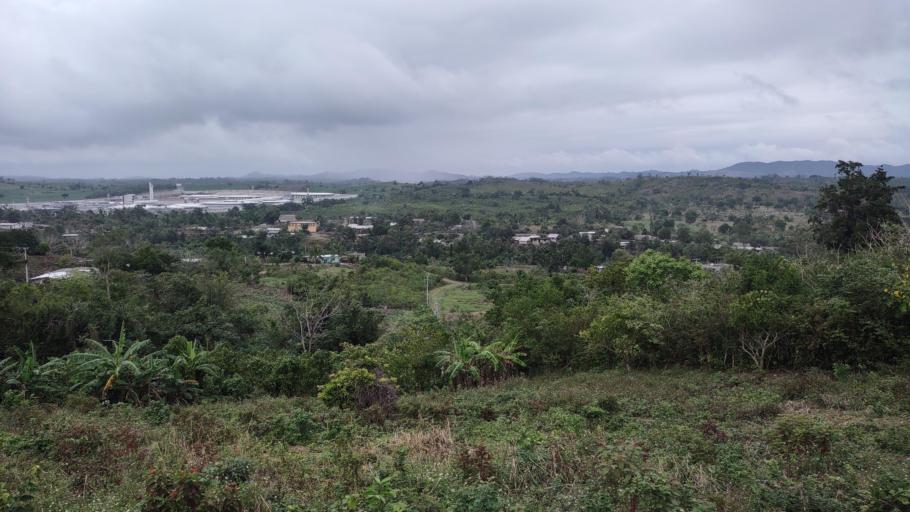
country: MX
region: Veracruz
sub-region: Papantla
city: El Chote
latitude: 20.3922
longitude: -97.3943
